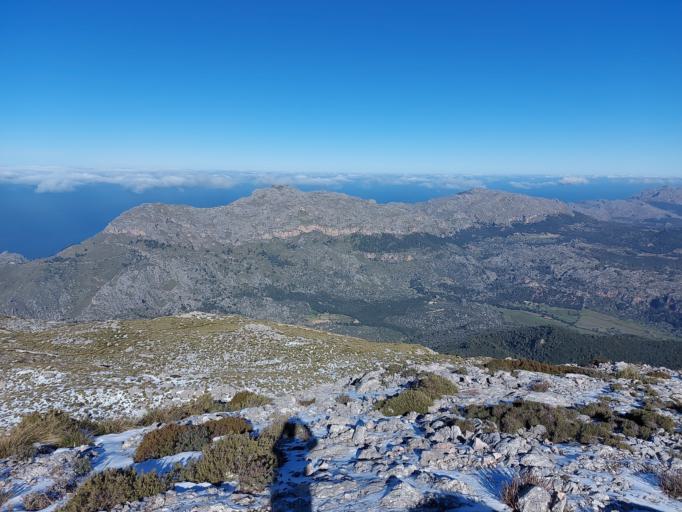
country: ES
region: Balearic Islands
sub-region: Illes Balears
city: Escorca
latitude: 39.8133
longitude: 2.8568
